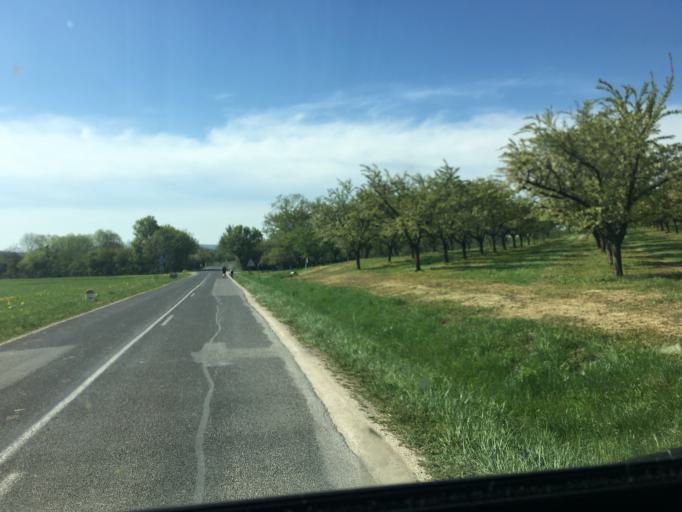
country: FR
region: Lorraine
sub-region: Departement de la Meuse
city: Vigneulles-les-Hattonchatel
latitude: 48.9305
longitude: 5.6910
